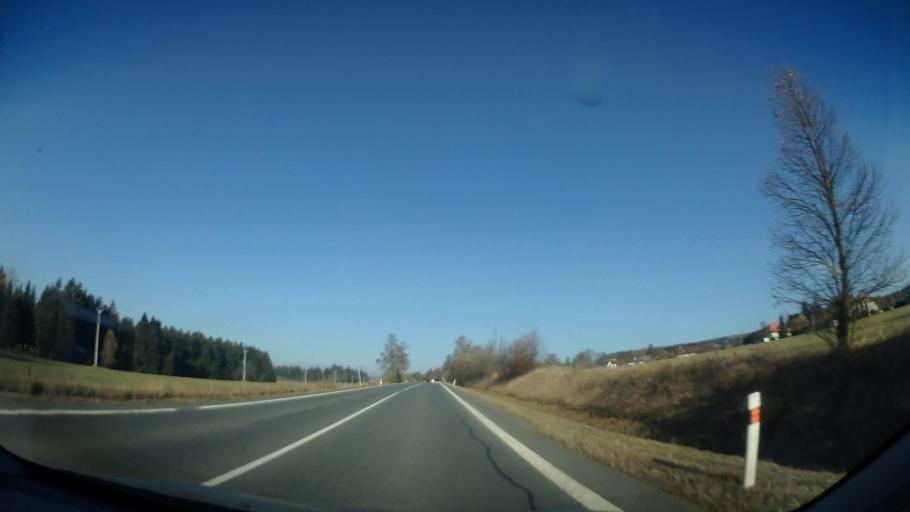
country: CZ
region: Vysocina
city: Zd'ar nad Sazavou Druhy
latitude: 49.6430
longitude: 15.9147
